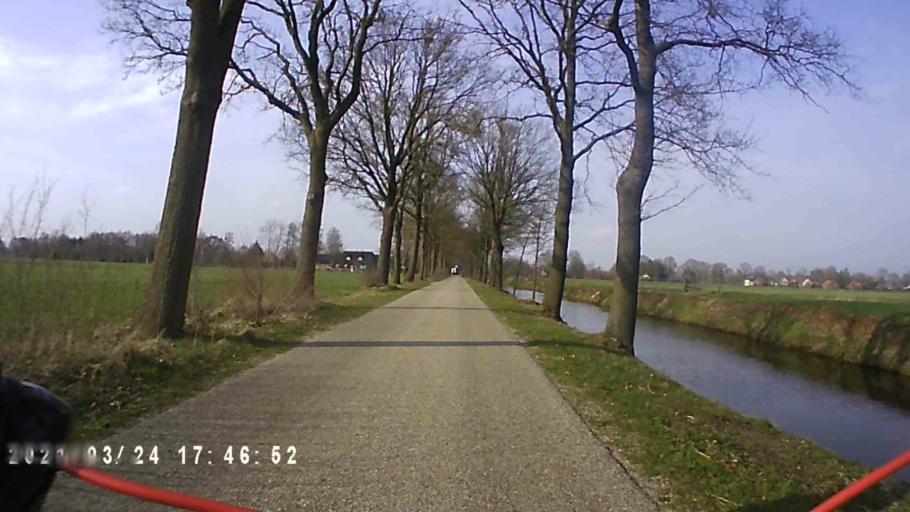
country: NL
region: Groningen
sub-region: Gemeente Leek
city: Leek
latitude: 53.1129
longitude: 6.3363
